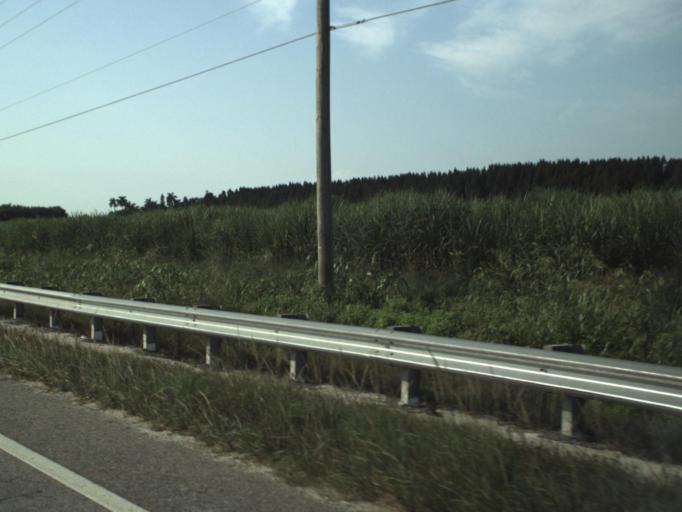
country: US
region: Florida
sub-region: Hendry County
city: Clewiston
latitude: 26.7236
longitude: -80.8477
